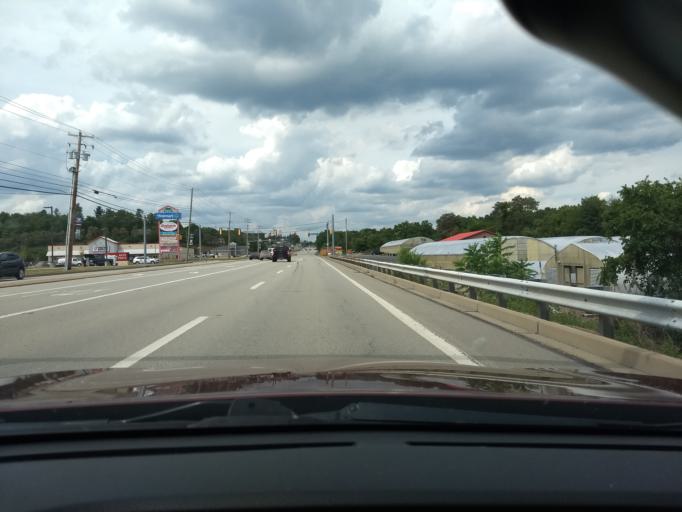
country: US
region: Pennsylvania
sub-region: Armstrong County
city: Freeport
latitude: 40.6449
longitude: -79.7098
